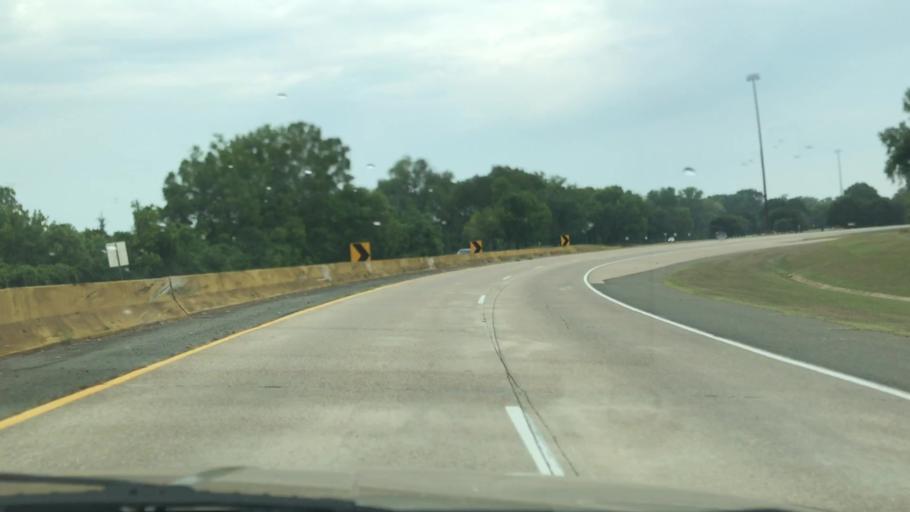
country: US
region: Louisiana
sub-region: Bossier Parish
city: Bossier City
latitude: 32.5074
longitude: -93.7252
